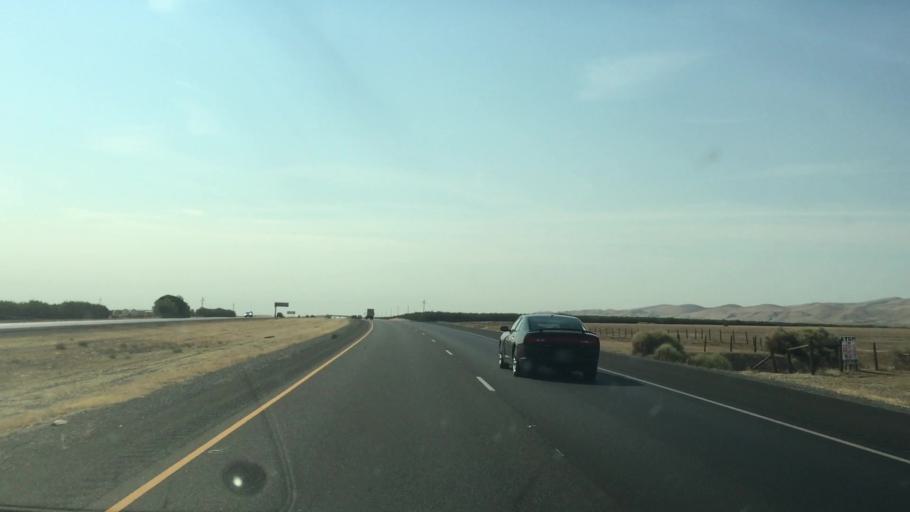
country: US
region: California
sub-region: Fresno County
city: Mendota
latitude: 36.6219
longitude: -120.6089
